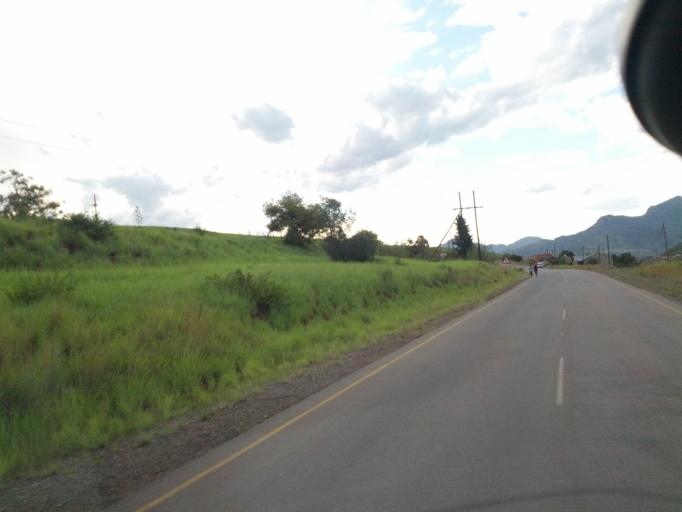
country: LS
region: Qacha's Nek
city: Qacha's Nek
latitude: -30.0930
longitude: 28.6453
